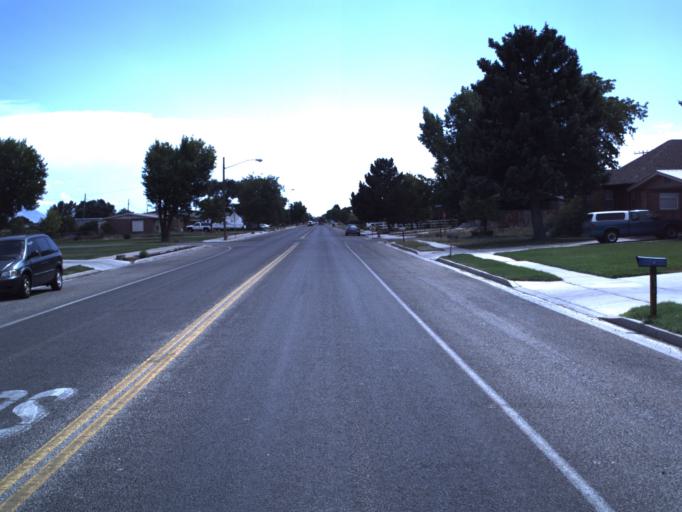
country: US
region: Utah
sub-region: Box Elder County
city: Garland
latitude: 41.7346
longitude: -112.1625
